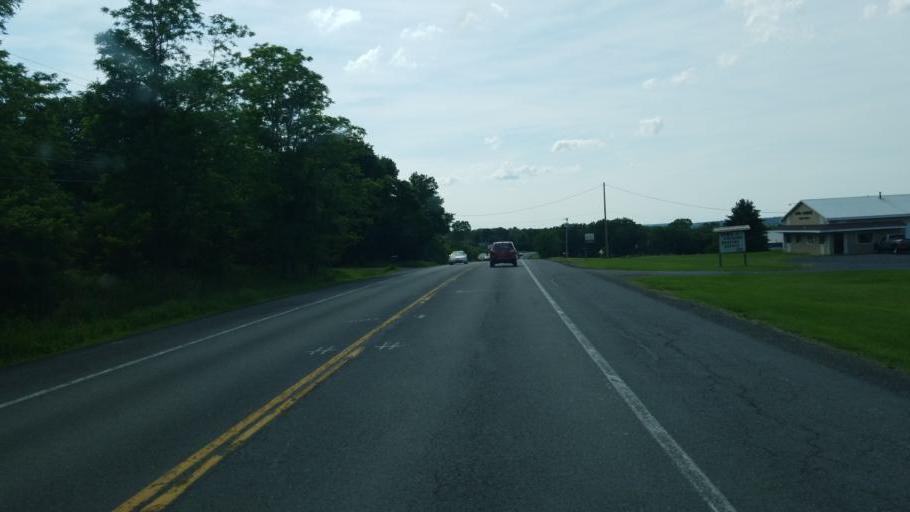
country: US
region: New York
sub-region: Ontario County
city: Canandaigua
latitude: 42.8659
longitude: -77.2237
